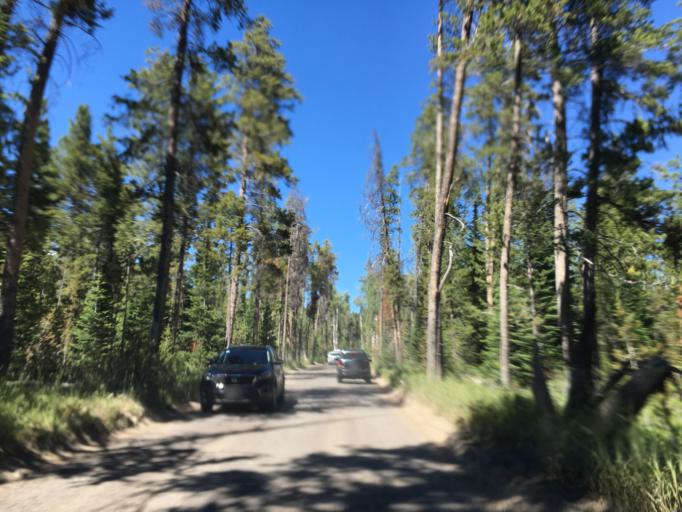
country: US
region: Wyoming
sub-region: Teton County
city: Moose Wilson Road
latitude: 43.6173
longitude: -110.7904
